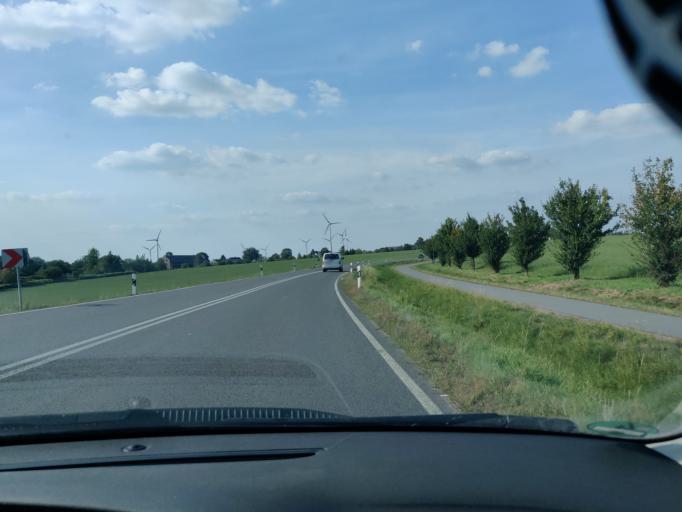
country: DE
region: Saxony
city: Erlau
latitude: 51.0031
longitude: 12.9513
